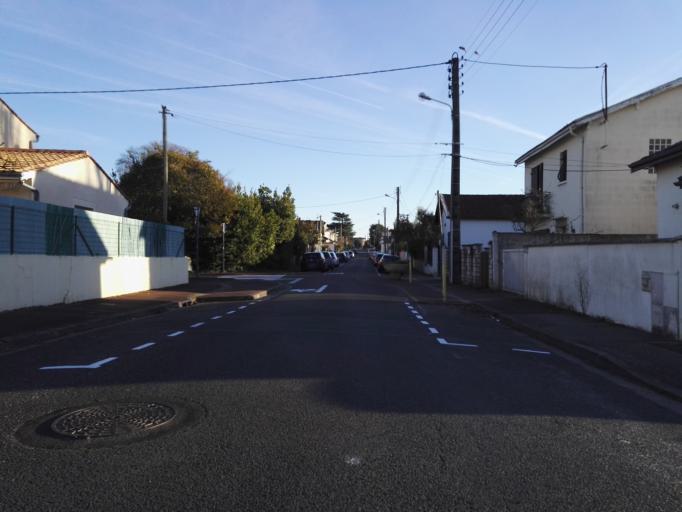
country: FR
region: Aquitaine
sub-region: Departement de la Gironde
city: Talence
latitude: 44.8149
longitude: -0.5984
